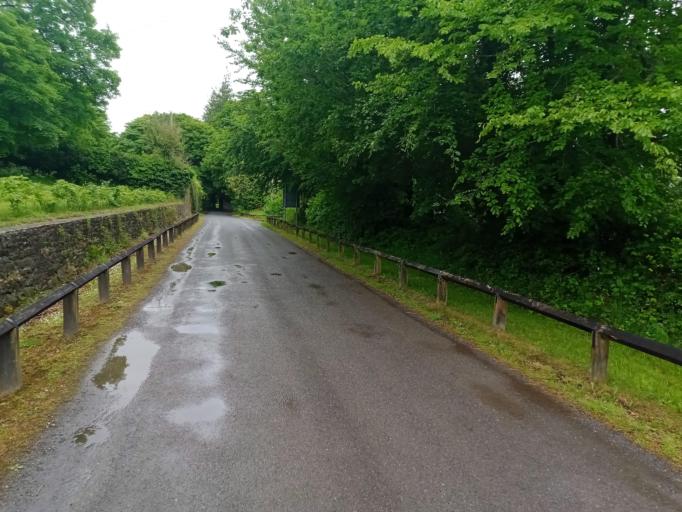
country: IE
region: Leinster
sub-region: Kilkenny
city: Thomastown
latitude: 52.4769
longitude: -7.0580
